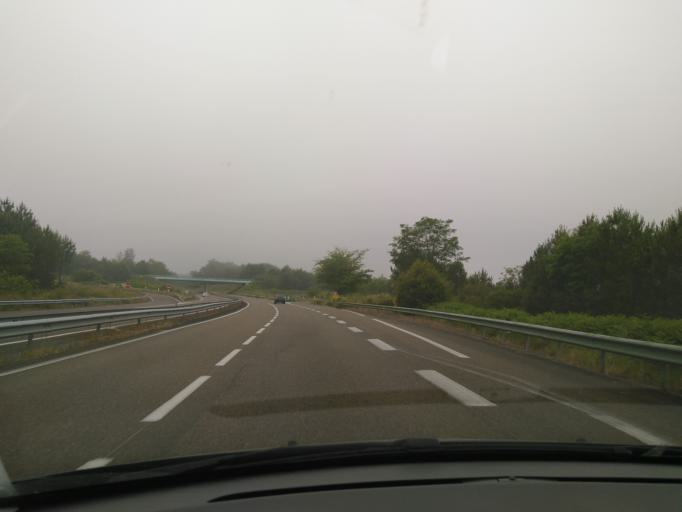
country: FR
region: Aquitaine
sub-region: Departement des Landes
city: Meilhan
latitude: 43.8639
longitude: -0.6885
